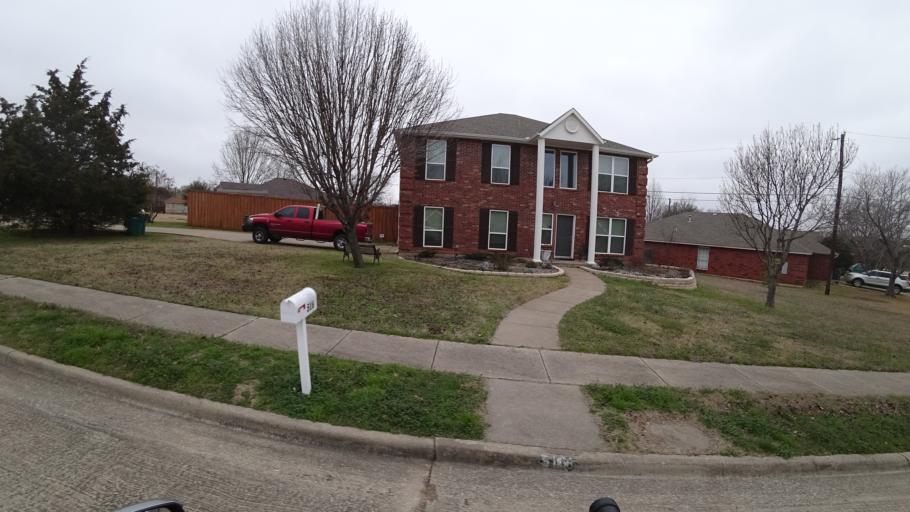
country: US
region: Texas
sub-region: Denton County
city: Lewisville
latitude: 33.0552
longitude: -97.0048
